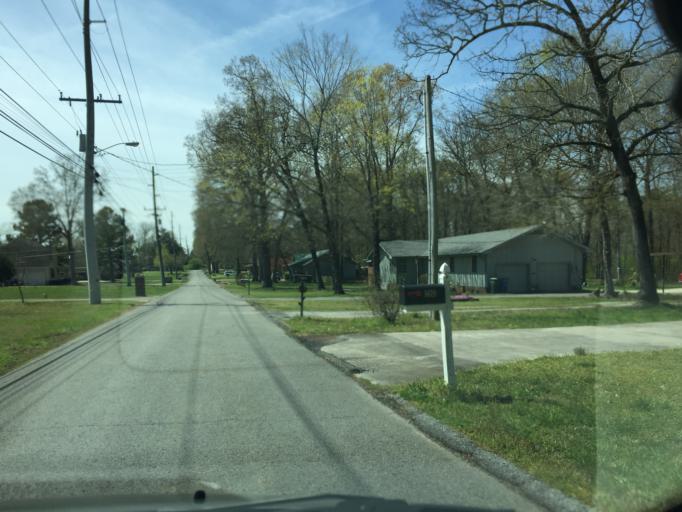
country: US
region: Tennessee
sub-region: Hamilton County
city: Middle Valley
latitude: 35.1627
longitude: -85.2082
